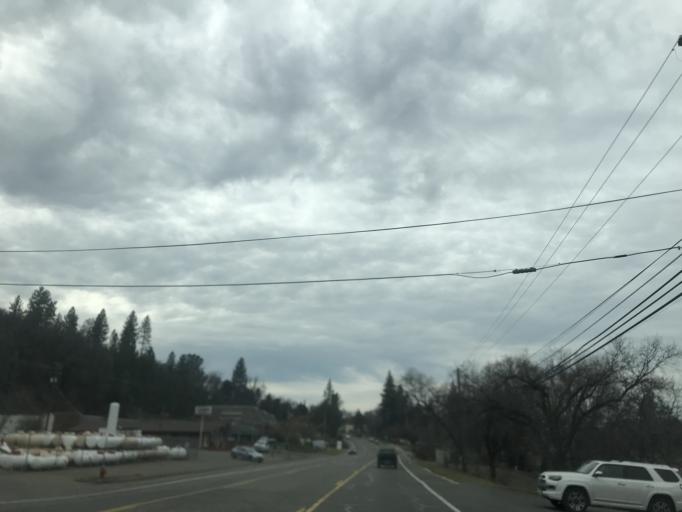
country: US
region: California
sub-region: El Dorado County
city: Placerville
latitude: 38.7327
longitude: -120.8318
